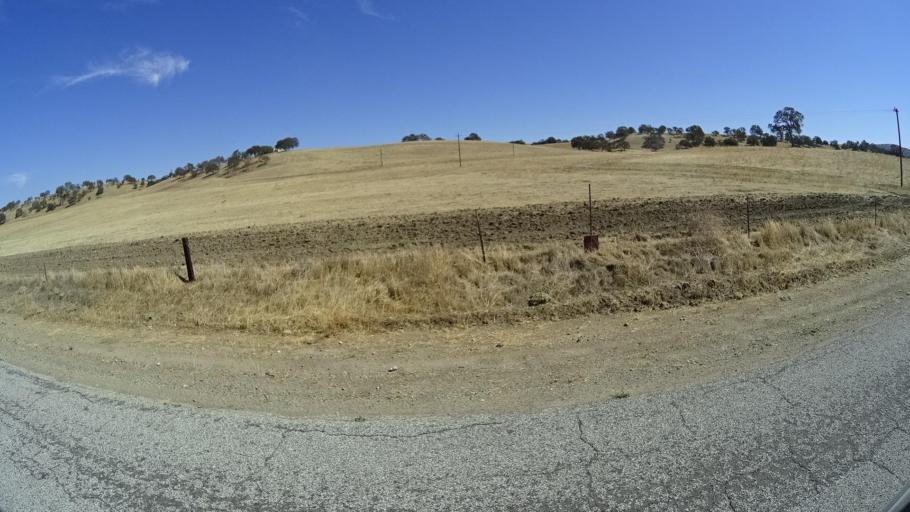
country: US
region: California
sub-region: San Luis Obispo County
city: San Miguel
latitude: 35.8378
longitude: -120.7020
